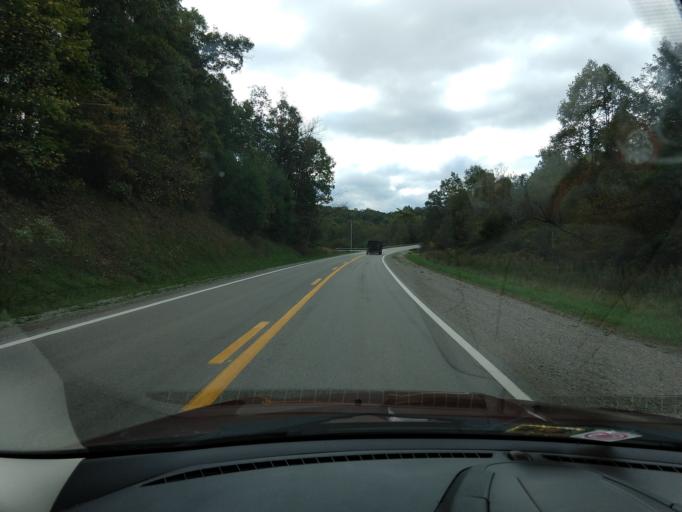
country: US
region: West Virginia
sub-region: Barbour County
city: Belington
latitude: 39.0373
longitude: -79.9551
